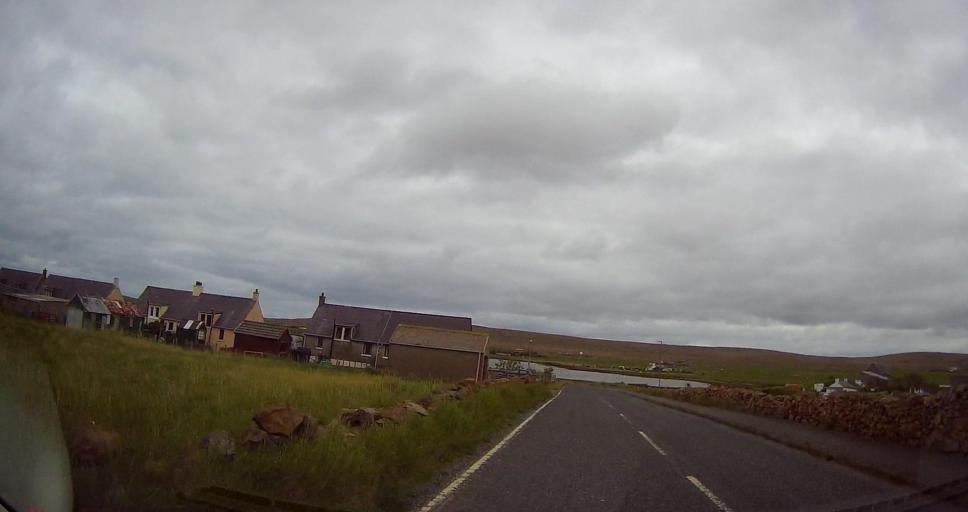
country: GB
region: Scotland
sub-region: Shetland Islands
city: Shetland
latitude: 60.7594
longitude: -0.8587
